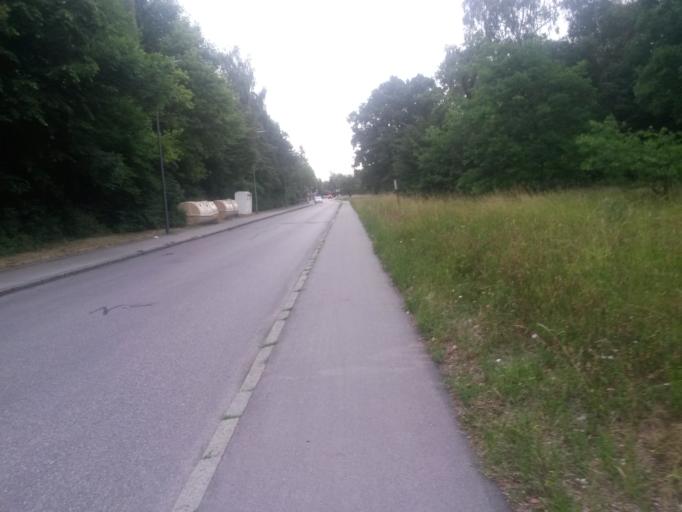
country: DE
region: Bavaria
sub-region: Upper Bavaria
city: Neubiberg
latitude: 48.1035
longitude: 11.6662
